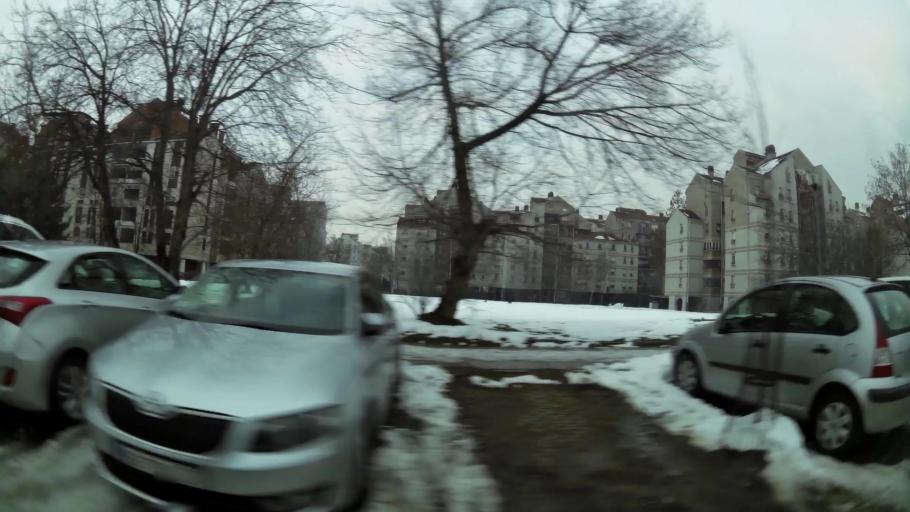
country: RS
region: Central Serbia
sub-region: Belgrade
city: Zemun
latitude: 44.8163
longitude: 20.3802
